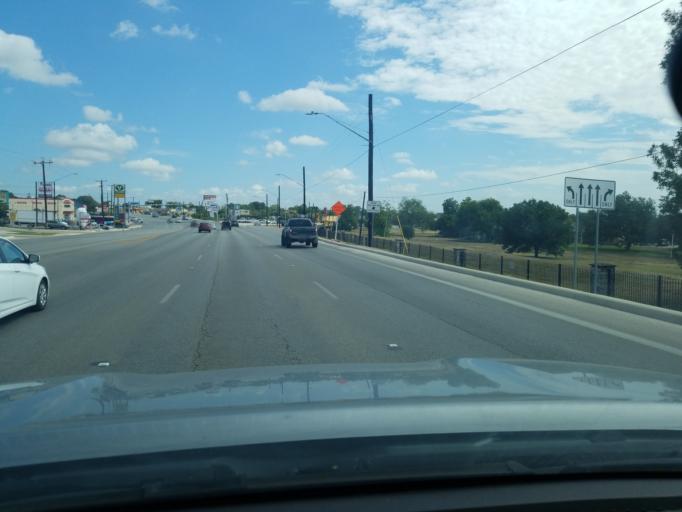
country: US
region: Texas
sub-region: Bexar County
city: Terrell Hills
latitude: 29.4830
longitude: -98.4311
